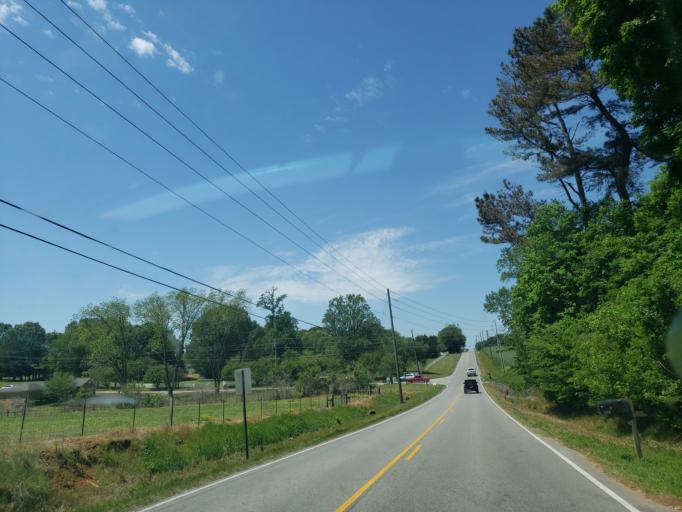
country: US
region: Alabama
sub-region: Madison County
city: Hazel Green
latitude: 34.9322
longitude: -86.5339
